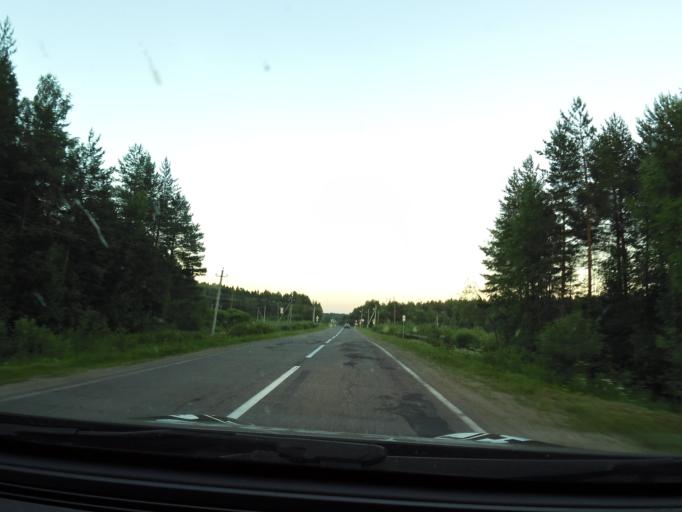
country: RU
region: Jaroslavl
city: Lyubim
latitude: 58.3347
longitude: 40.8894
